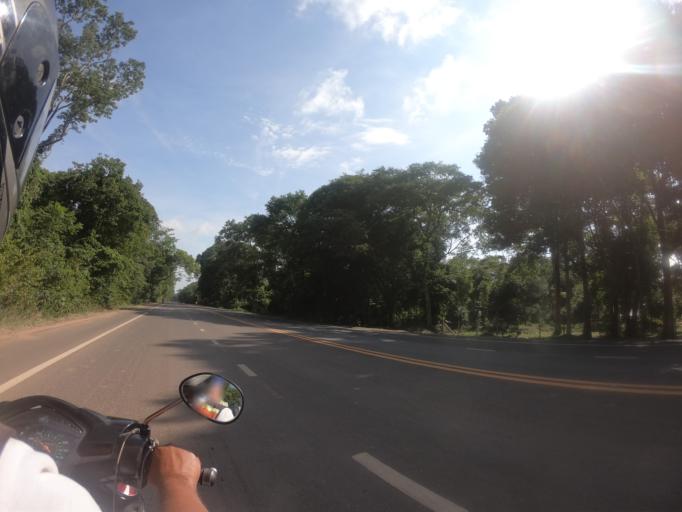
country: TH
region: Surin
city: Kap Choeng
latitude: 14.4421
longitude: 103.7007
